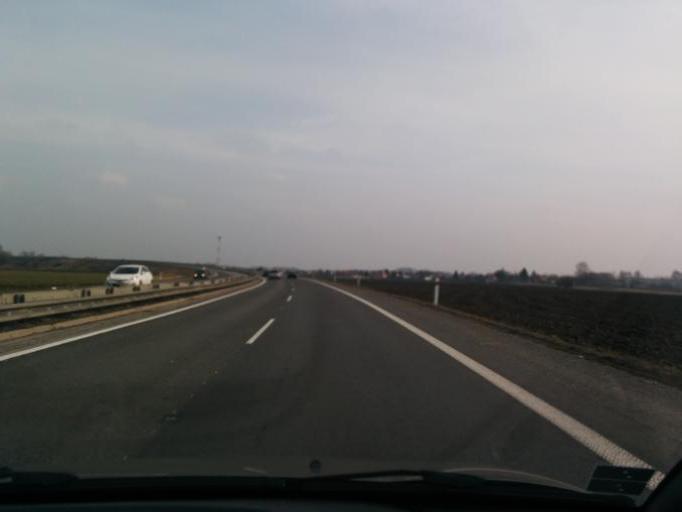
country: SK
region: Trnavsky
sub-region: Okres Galanta
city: Galanta
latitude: 48.2560
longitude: 17.7678
